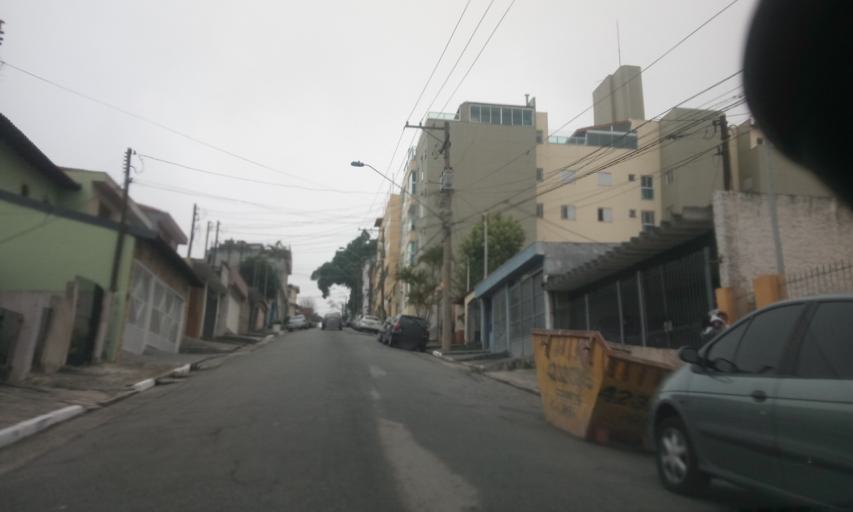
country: BR
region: Sao Paulo
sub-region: Sao Caetano Do Sul
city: Sao Caetano do Sul
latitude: -23.6440
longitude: -46.5688
